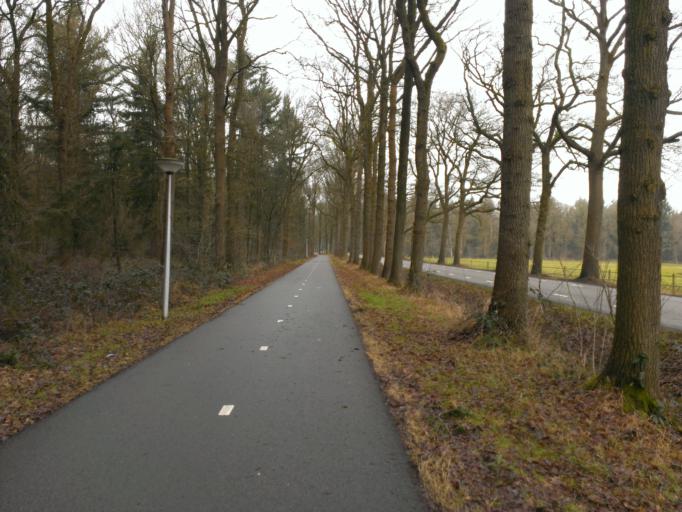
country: NL
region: Drenthe
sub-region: Gemeente Hoogeveen
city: Hoogeveen
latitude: 52.7496
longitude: 6.4667
